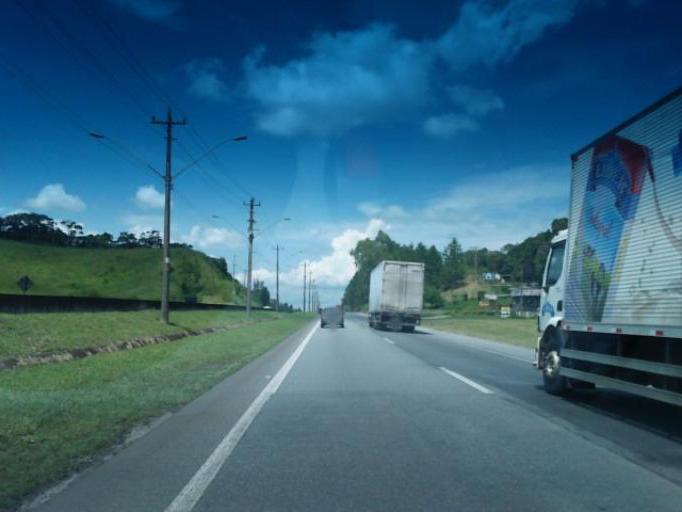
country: BR
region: Sao Paulo
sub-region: Sao Lourenco Da Serra
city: Sao Lourenco da Serra
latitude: -23.8666
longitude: -46.9519
